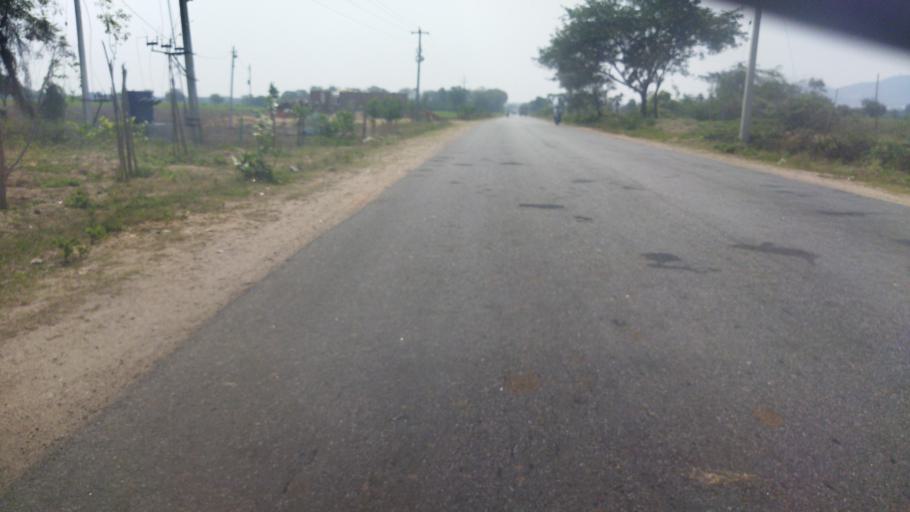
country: IN
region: Telangana
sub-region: Nalgonda
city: Nalgonda
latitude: 17.0935
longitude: 79.2856
